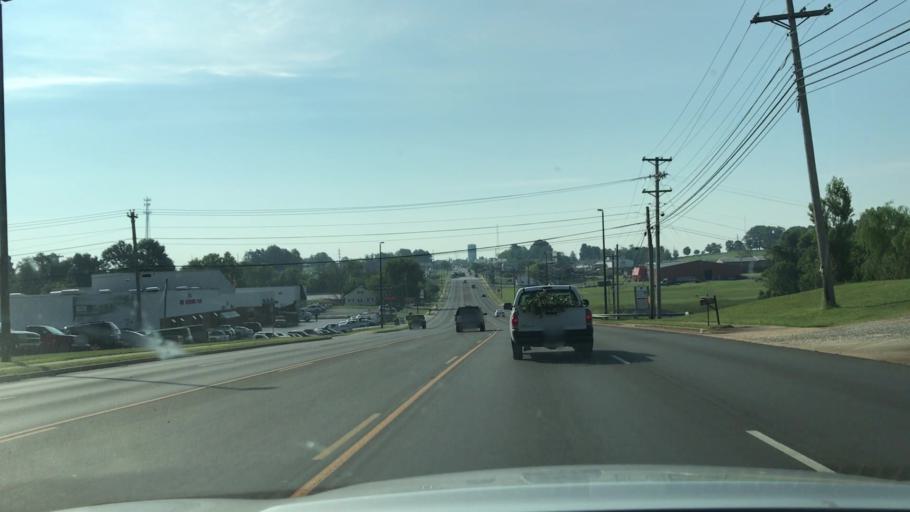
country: US
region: Kentucky
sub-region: Barren County
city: Glasgow
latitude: 37.0054
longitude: -85.9321
